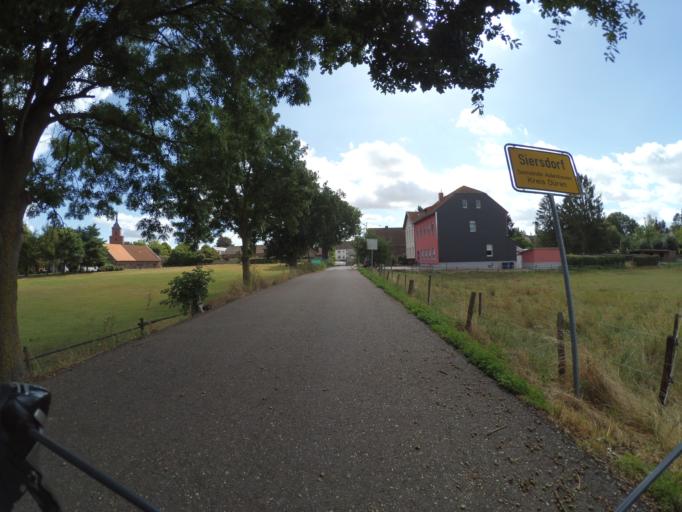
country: DE
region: North Rhine-Westphalia
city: Siersdorf
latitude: 50.8991
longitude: 6.2205
